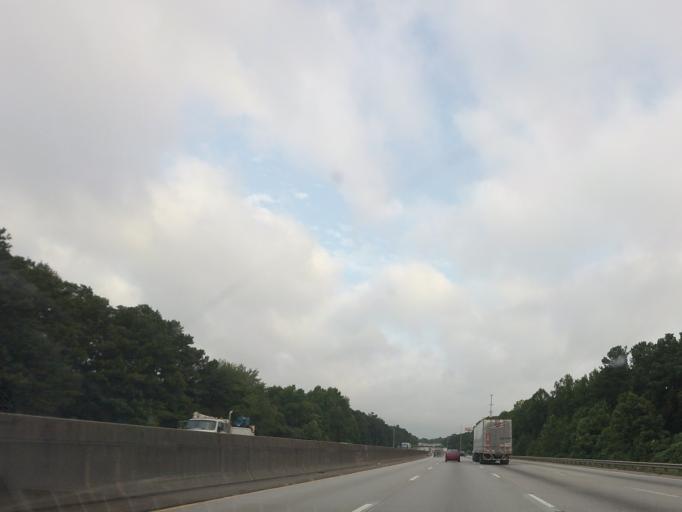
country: US
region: Georgia
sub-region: Clayton County
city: Morrow
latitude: 33.5526
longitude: -84.2928
